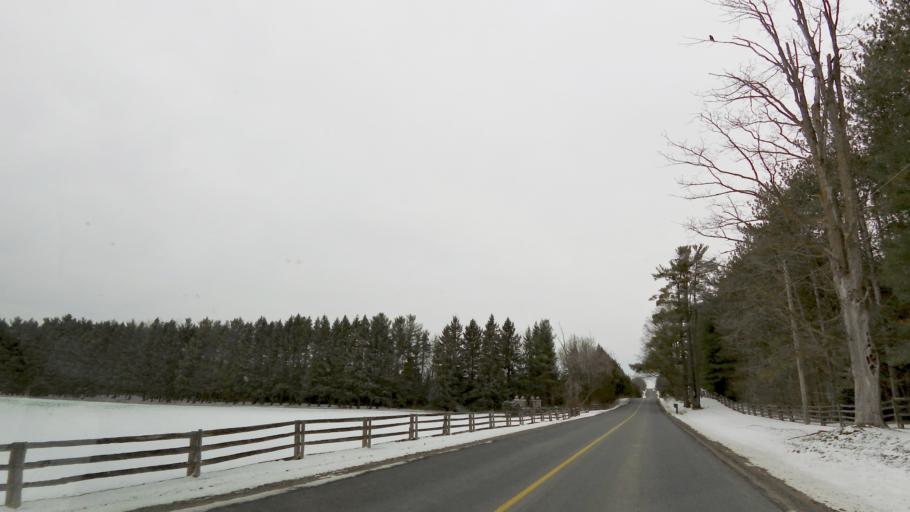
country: CA
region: Ontario
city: Bradford West Gwillimbury
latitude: 43.9483
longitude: -79.6380
